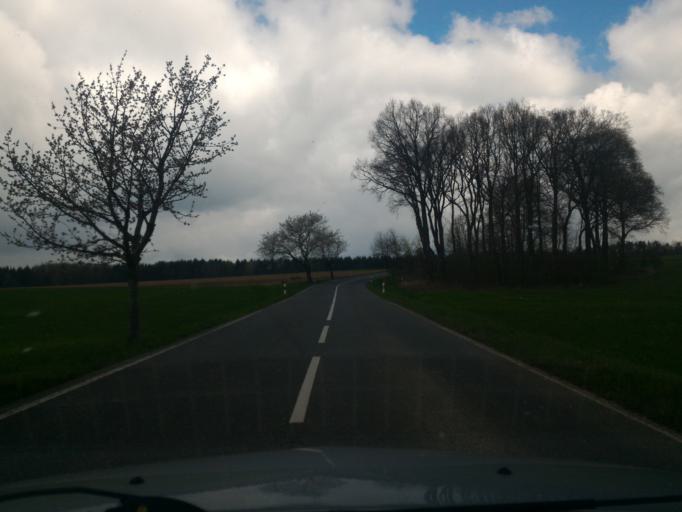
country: DE
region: Saxony
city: Hainewalde
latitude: 50.9267
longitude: 14.7037
